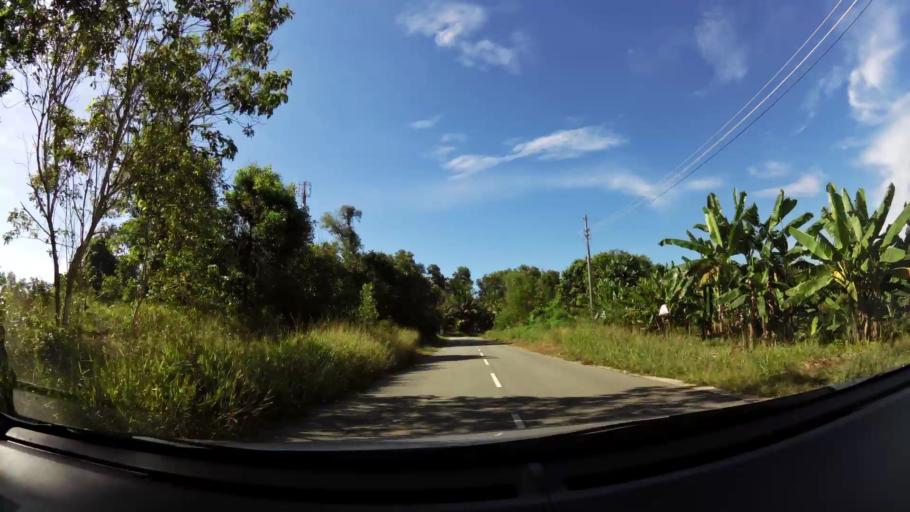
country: BN
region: Brunei and Muara
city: Bandar Seri Begawan
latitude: 4.9656
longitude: 114.9309
